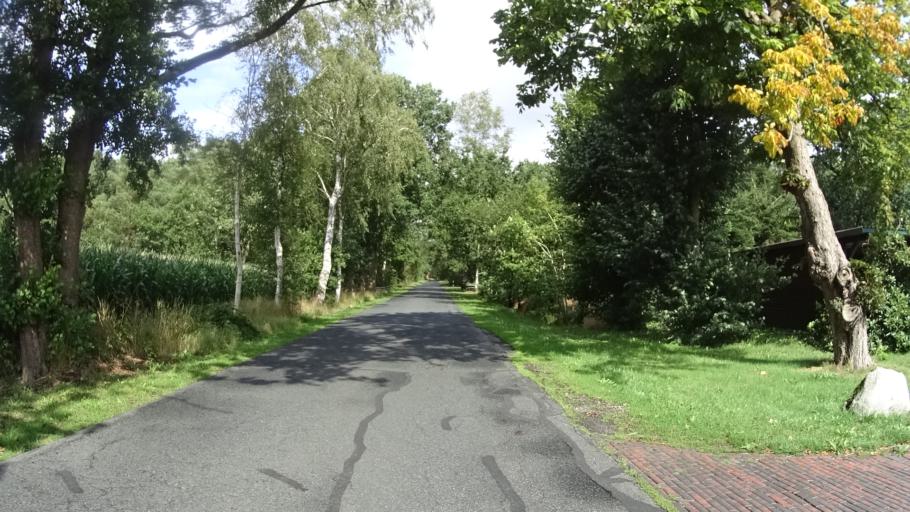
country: DE
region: Lower Saxony
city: Zetel
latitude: 53.3848
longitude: 7.8986
